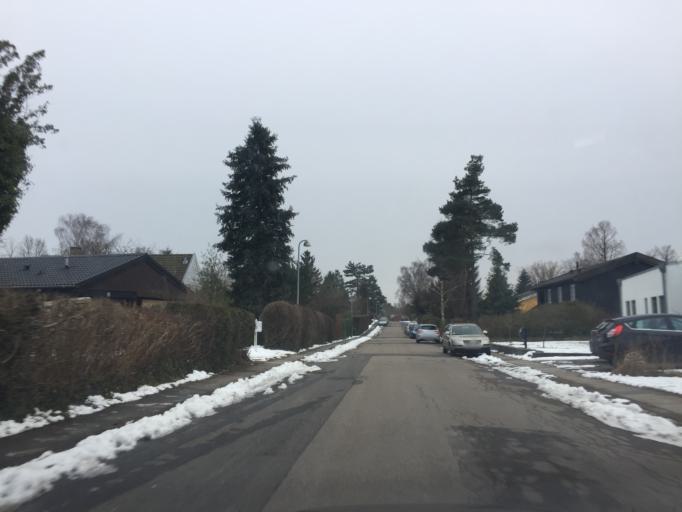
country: DK
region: Capital Region
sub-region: Fureso Kommune
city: Vaerlose
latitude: 55.7600
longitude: 12.4082
